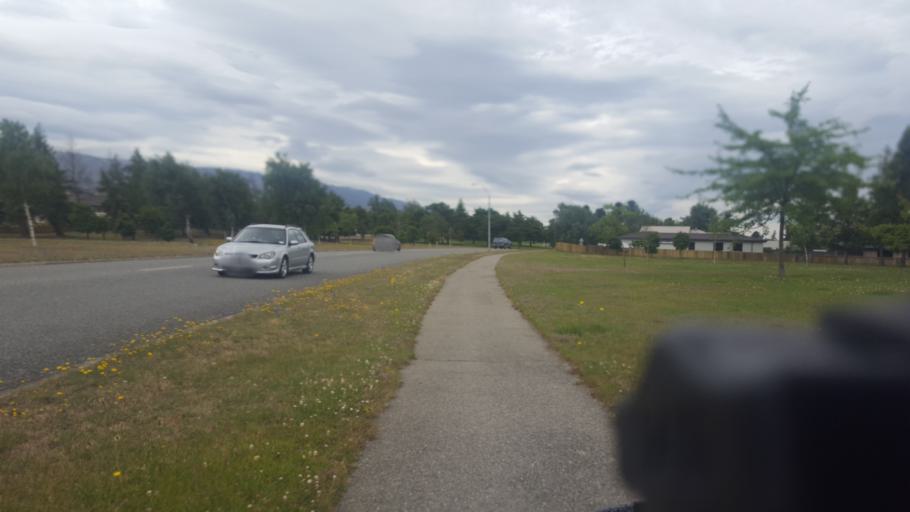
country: NZ
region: Otago
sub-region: Queenstown-Lakes District
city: Wanaka
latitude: -45.0488
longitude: 169.1847
